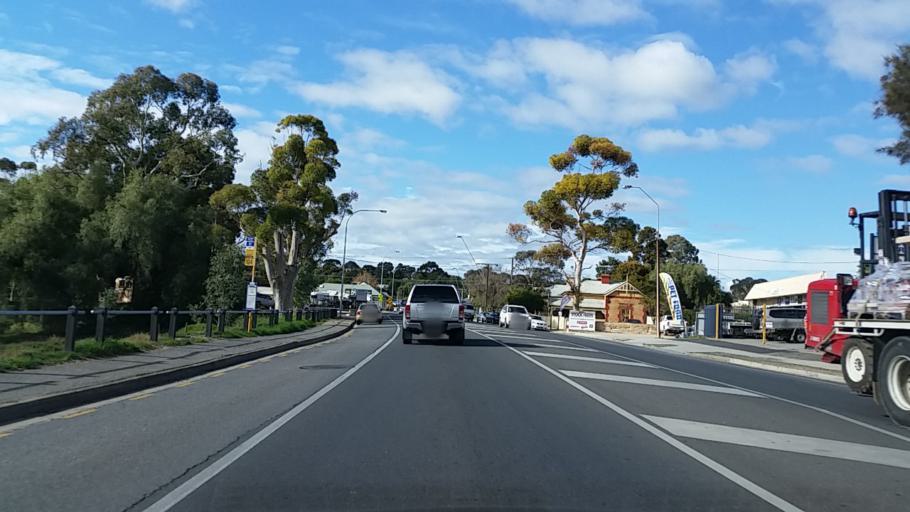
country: AU
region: South Australia
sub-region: Light
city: Willaston
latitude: -34.5927
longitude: 138.7467
